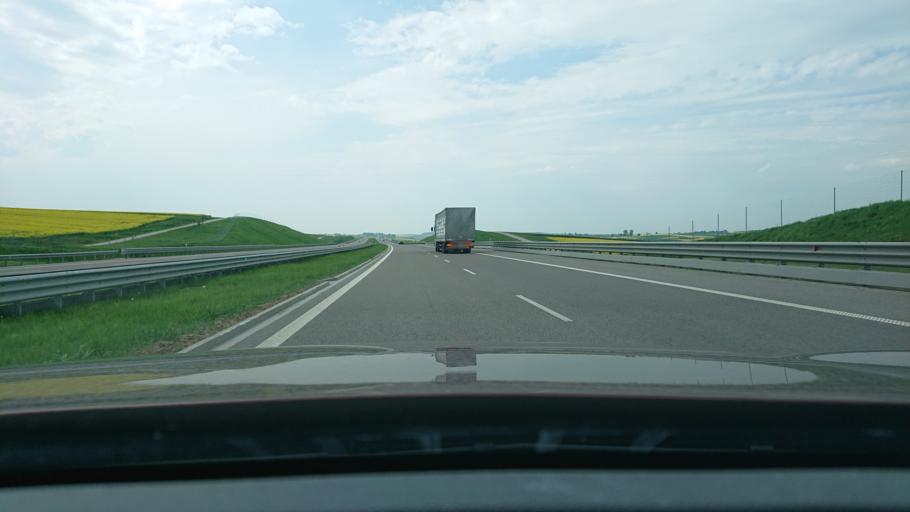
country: PL
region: Subcarpathian Voivodeship
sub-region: Powiat jaroslawski
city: Rokietnica
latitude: 49.9319
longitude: 22.7106
